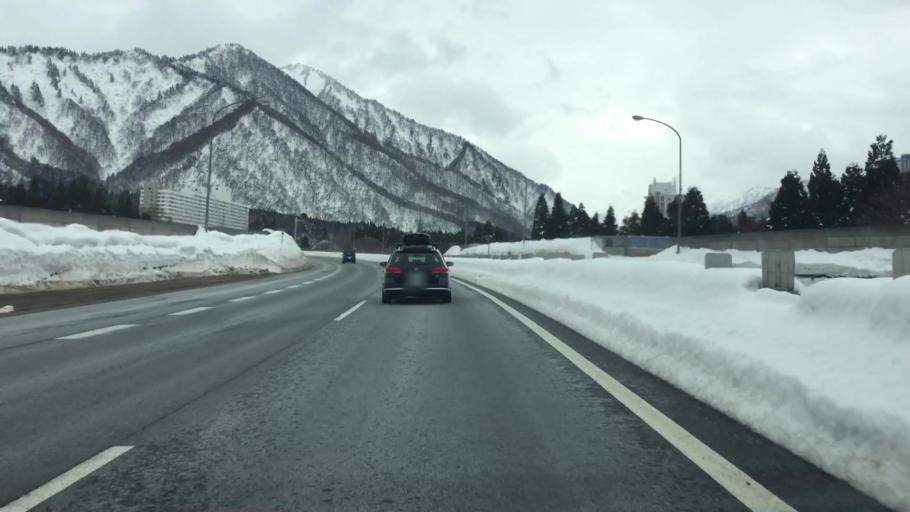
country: JP
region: Niigata
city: Shiozawa
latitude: 36.9087
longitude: 138.8417
